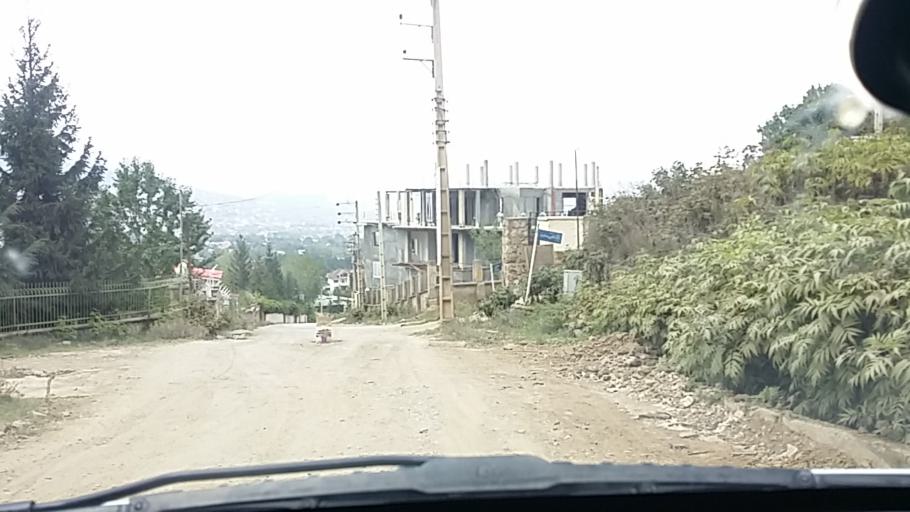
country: IR
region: Mazandaran
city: `Abbasabad
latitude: 36.4934
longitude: 51.1653
